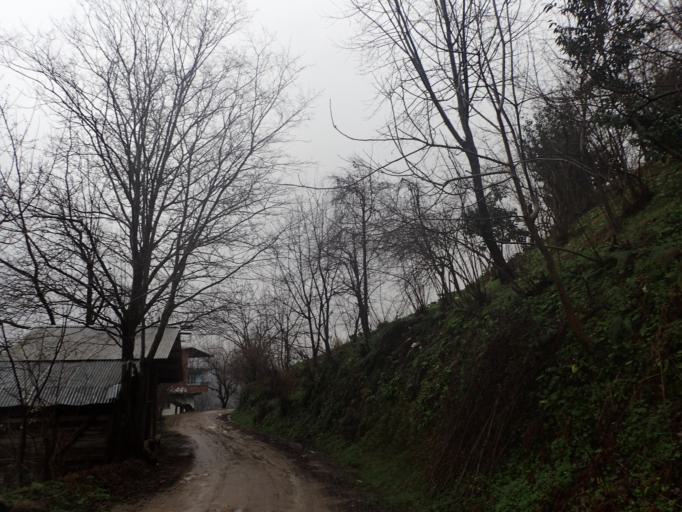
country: TR
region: Ordu
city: Camas
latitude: 40.9112
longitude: 37.5678
